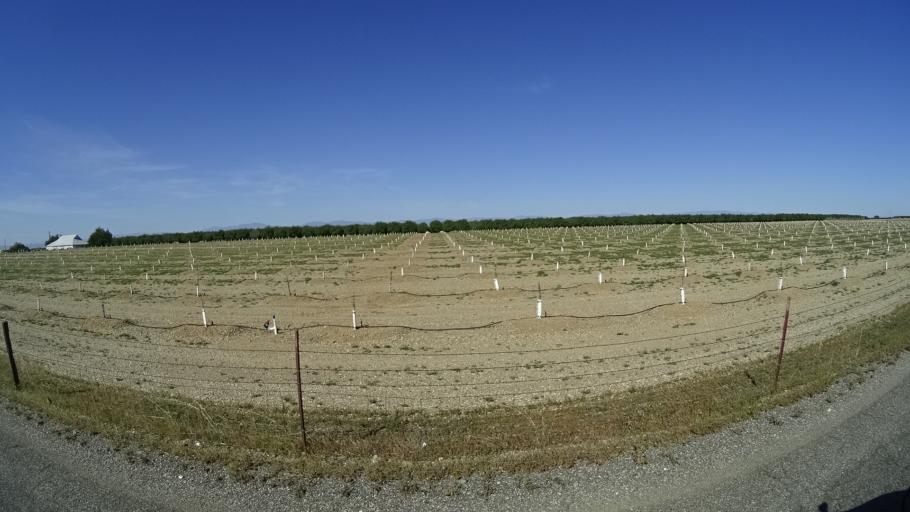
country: US
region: California
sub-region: Glenn County
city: Willows
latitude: 39.6135
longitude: -122.1566
